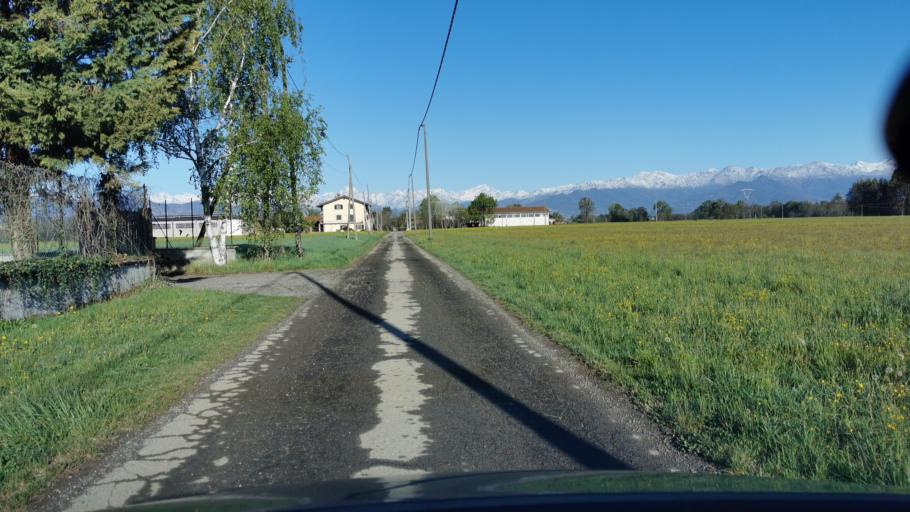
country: IT
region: Piedmont
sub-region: Provincia di Torino
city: Rivarossa
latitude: 45.2214
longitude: 7.7035
